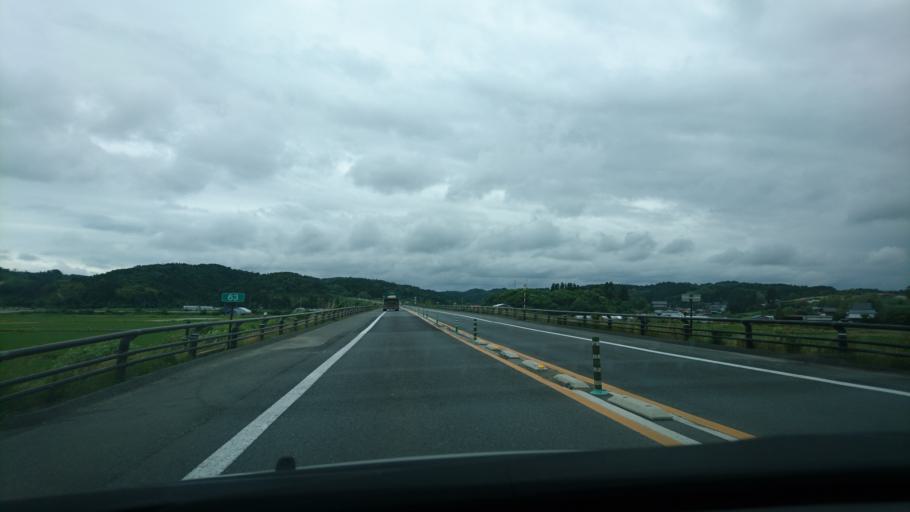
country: JP
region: Miyagi
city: Wakuya
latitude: 38.6532
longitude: 141.2640
